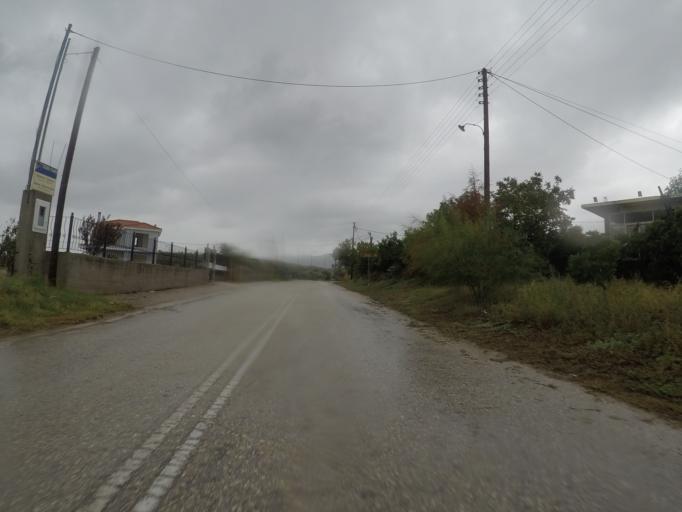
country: GR
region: Peloponnese
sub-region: Nomos Korinthias
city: Arkhaia Korinthos
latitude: 37.9018
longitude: 22.8872
